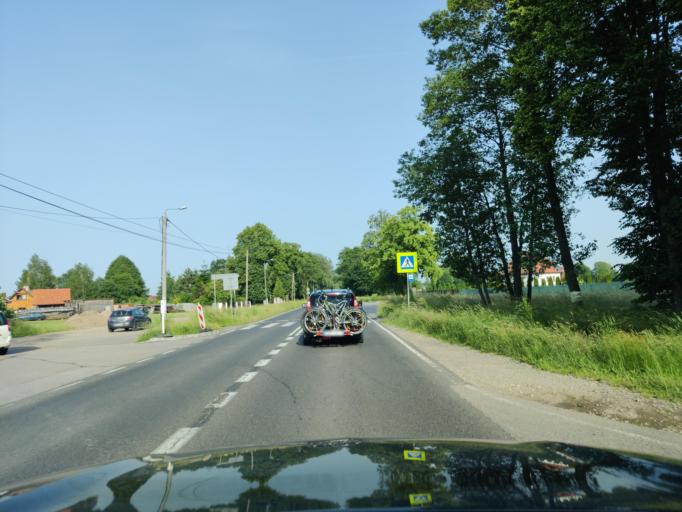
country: PL
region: Masovian Voivodeship
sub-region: Powiat wegrowski
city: Lochow
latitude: 52.5508
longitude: 21.6209
